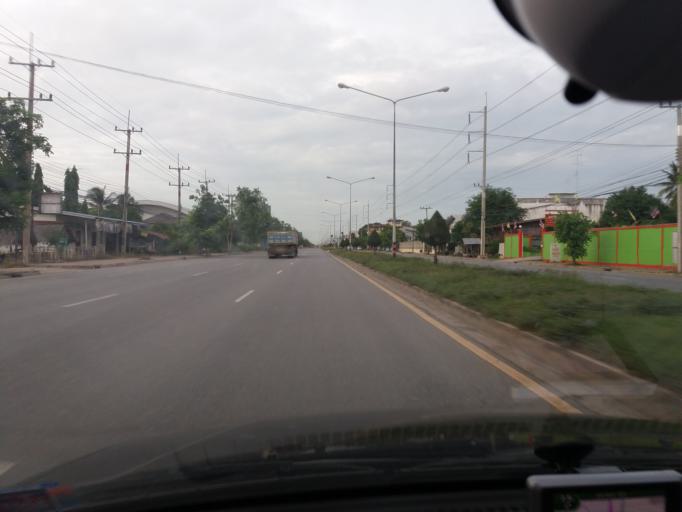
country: TH
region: Suphan Buri
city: U Thong
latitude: 14.3953
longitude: 99.8956
